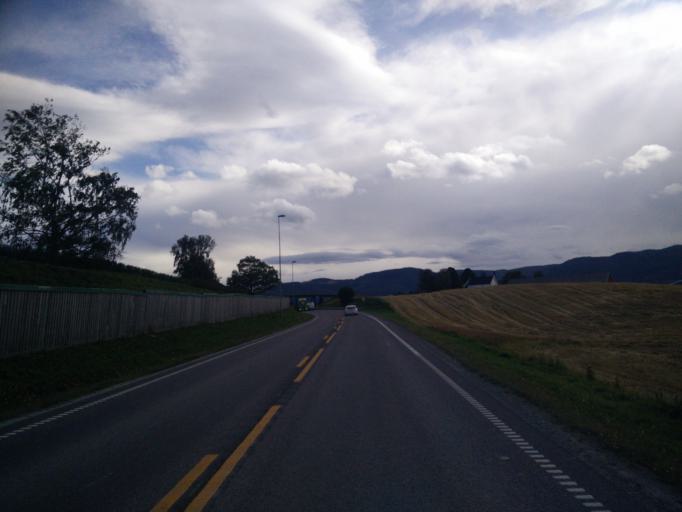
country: NO
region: Sor-Trondelag
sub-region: Melhus
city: Melhus
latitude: 63.3243
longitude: 10.2915
